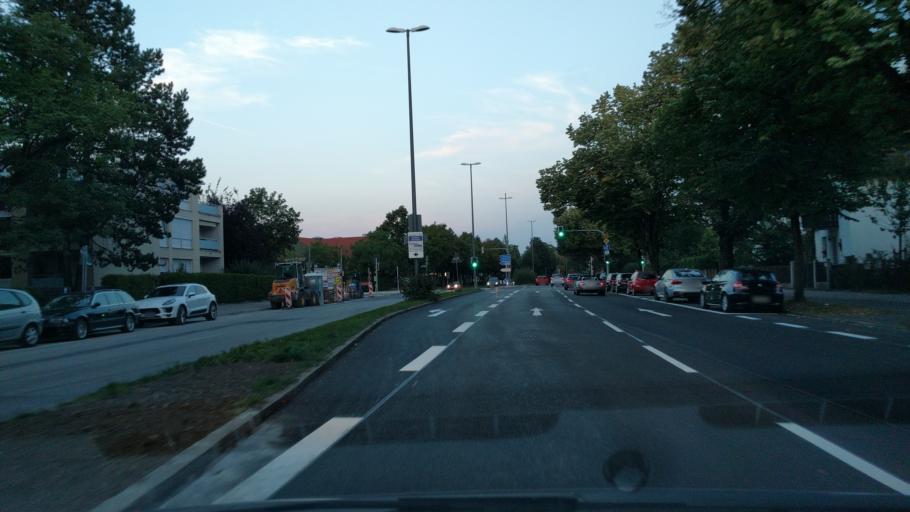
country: DE
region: Bavaria
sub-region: Upper Bavaria
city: Bogenhausen
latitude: 48.1249
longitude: 11.6530
